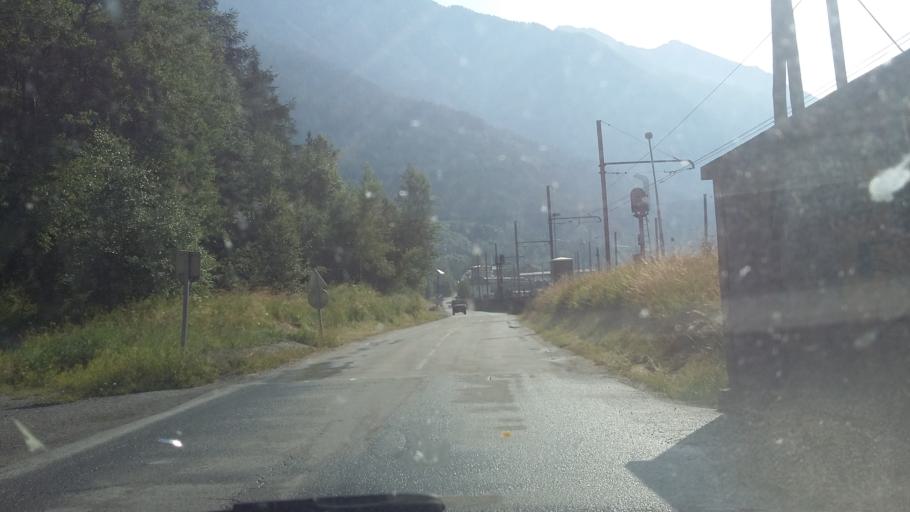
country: FR
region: Rhone-Alpes
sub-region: Departement de la Savoie
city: Modane
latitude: 45.1923
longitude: 6.6587
